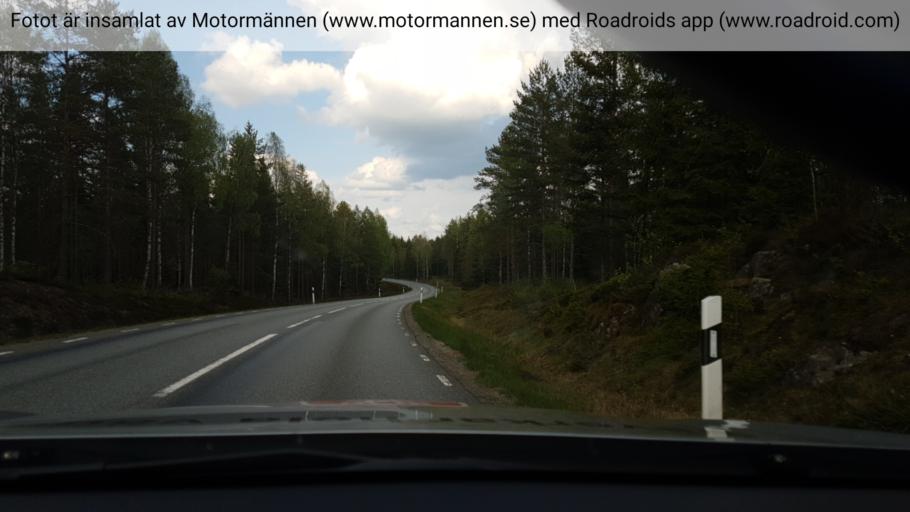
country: SE
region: Joenkoeping
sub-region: Gnosjo Kommun
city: Hillerstorp
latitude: 57.3729
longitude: 13.9658
